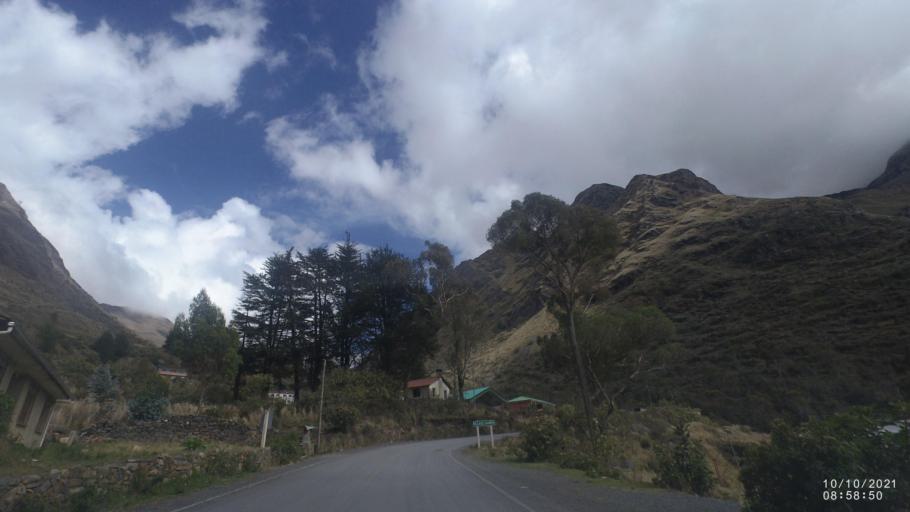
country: BO
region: La Paz
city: Quime
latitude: -16.9975
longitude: -67.2588
